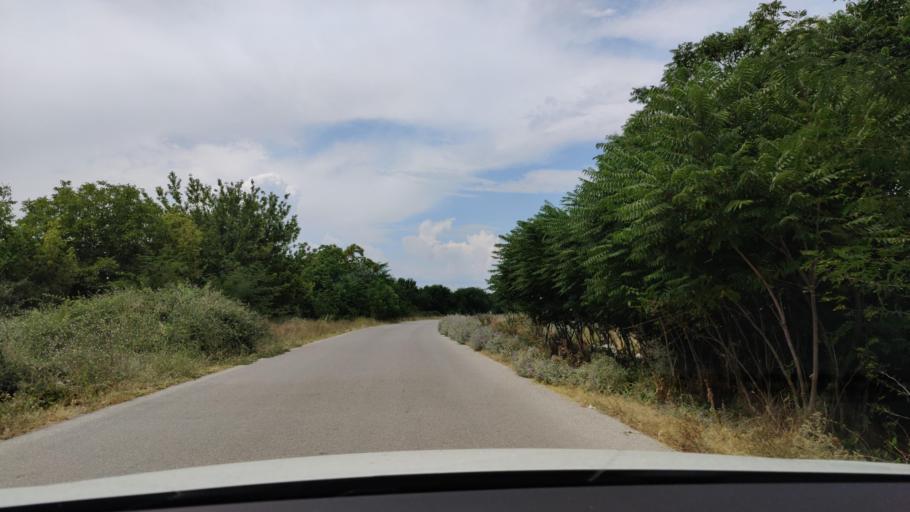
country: GR
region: Central Macedonia
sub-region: Nomos Serron
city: Serres
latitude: 41.0714
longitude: 23.5549
